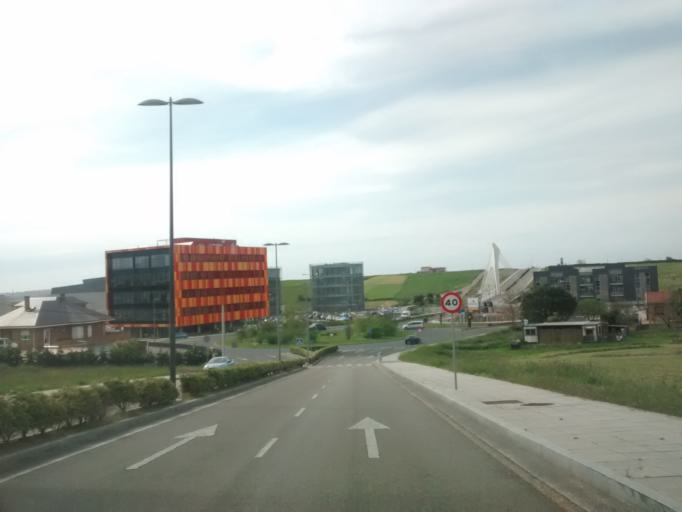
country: ES
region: Cantabria
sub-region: Provincia de Cantabria
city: Santa Cruz de Bezana
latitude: 43.4514
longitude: -3.8695
